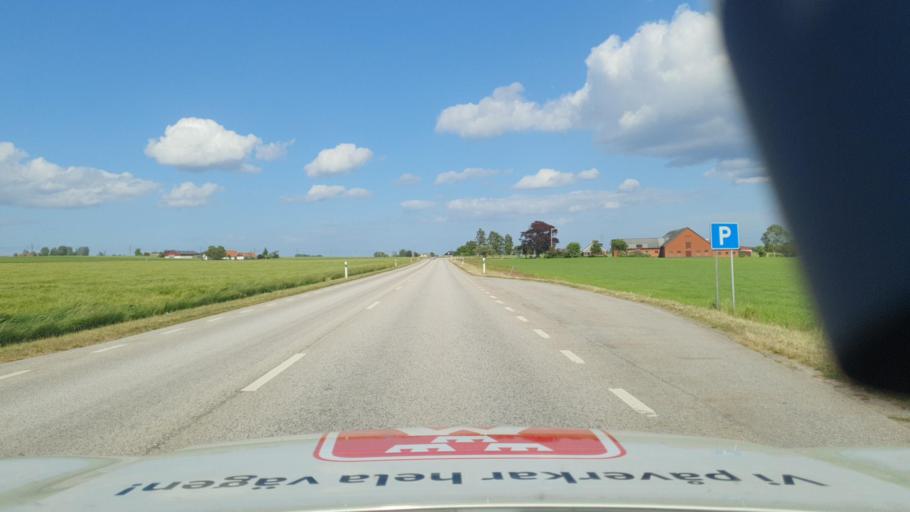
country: SE
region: Skane
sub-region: Simrishamns Kommun
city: Simrishamn
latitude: 55.5346
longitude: 14.2455
